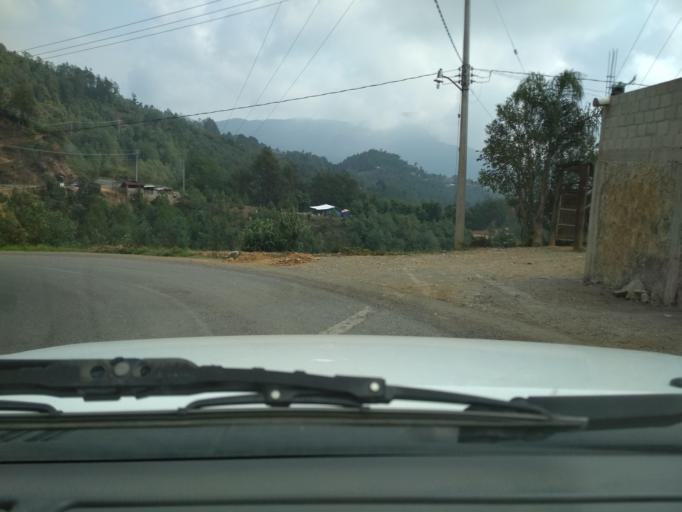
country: MX
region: Veracruz
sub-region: Camerino Z. Mendoza
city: Necoxtla
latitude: 18.7581
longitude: -97.1526
